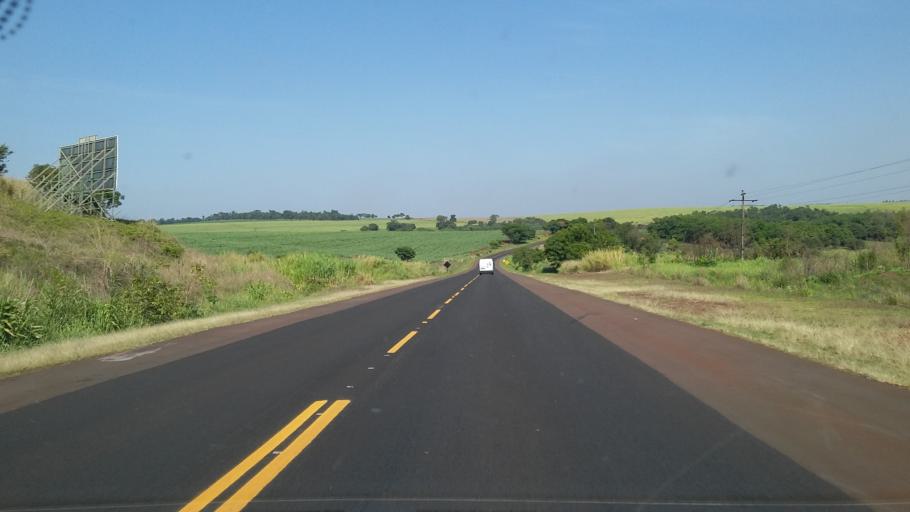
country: BR
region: Parana
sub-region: Bandeirantes
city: Bandeirantes
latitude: -23.1306
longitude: -50.4431
